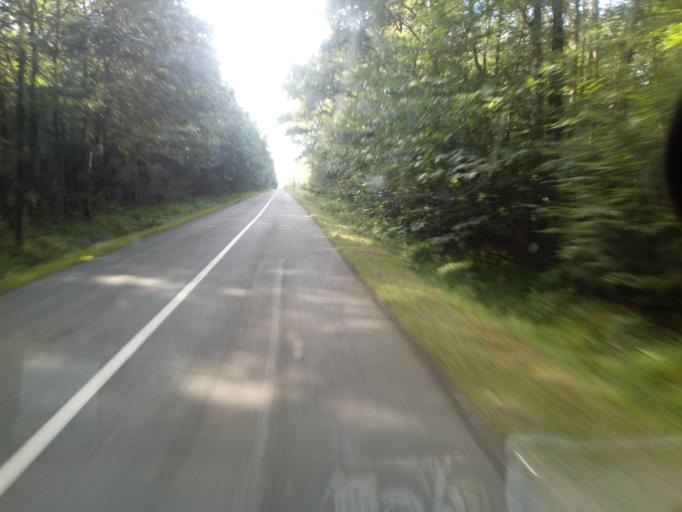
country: FR
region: Brittany
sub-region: Departement d'Ille-et-Vilaine
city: Paimpont
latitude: 48.0256
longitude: -2.1733
